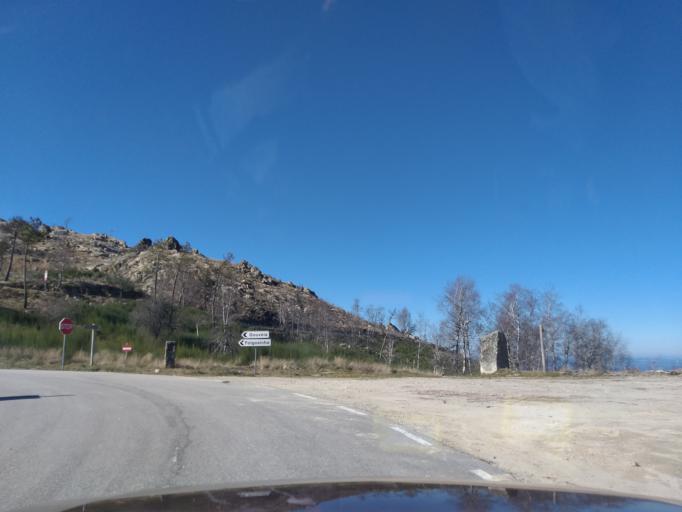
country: PT
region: Guarda
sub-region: Manteigas
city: Manteigas
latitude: 40.4813
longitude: -7.5144
